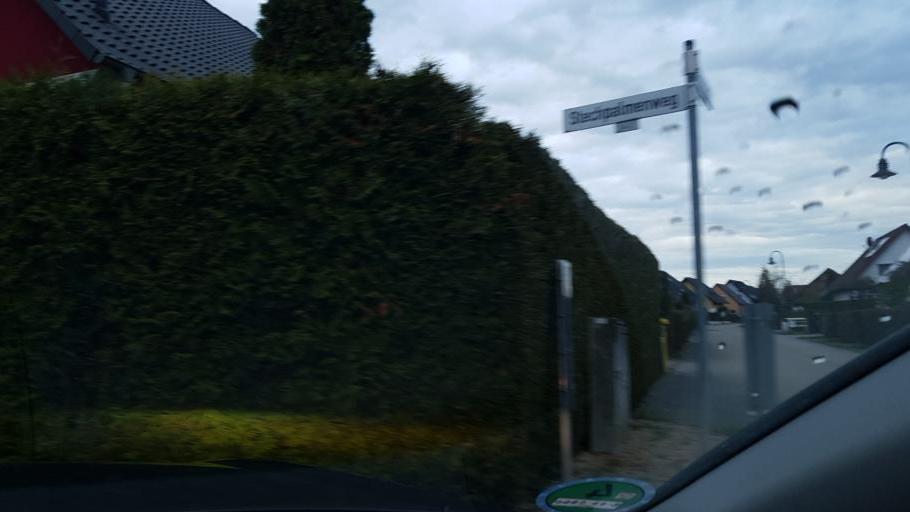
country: DE
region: Brandenburg
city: Frankfurt (Oder)
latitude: 52.3286
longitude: 14.5015
